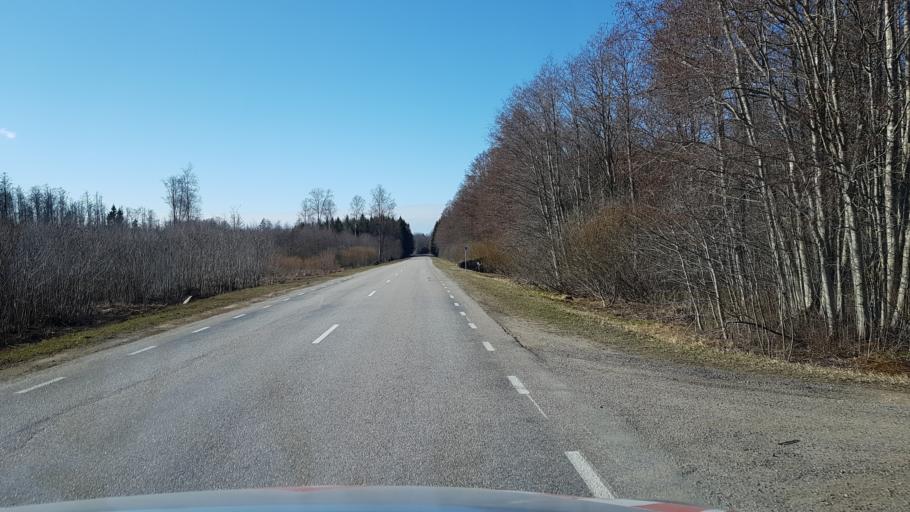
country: EE
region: Laeaene-Virumaa
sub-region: Haljala vald
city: Haljala
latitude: 59.5157
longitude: 26.0953
